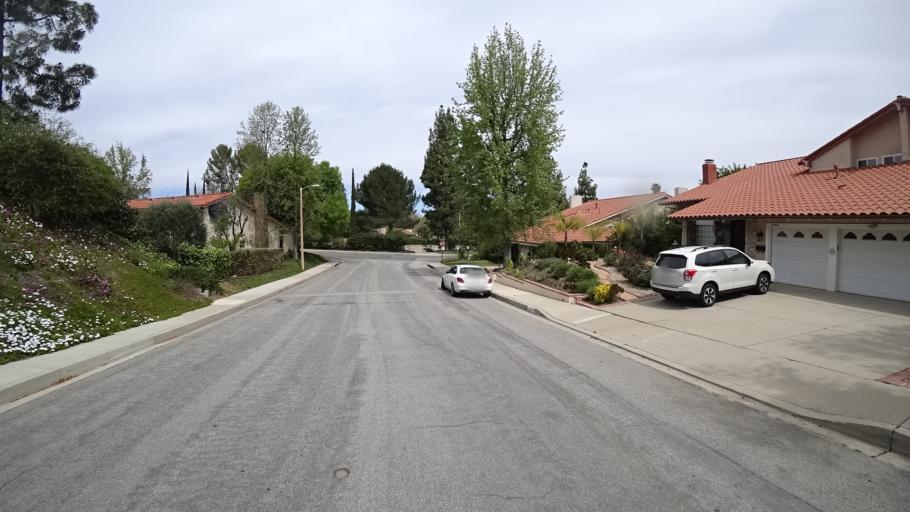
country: US
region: California
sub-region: Ventura County
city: Thousand Oaks
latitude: 34.1440
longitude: -118.8357
